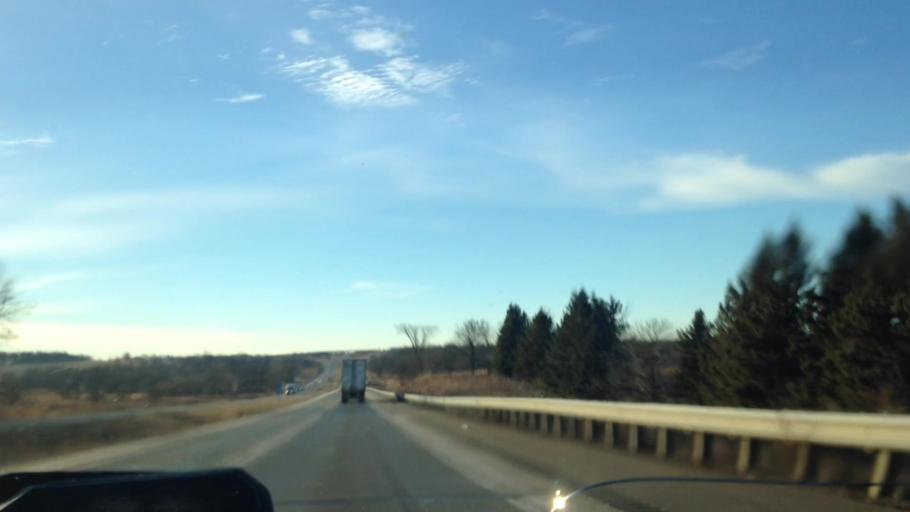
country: US
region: Wisconsin
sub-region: Dodge County
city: Theresa
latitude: 43.4907
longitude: -88.3671
